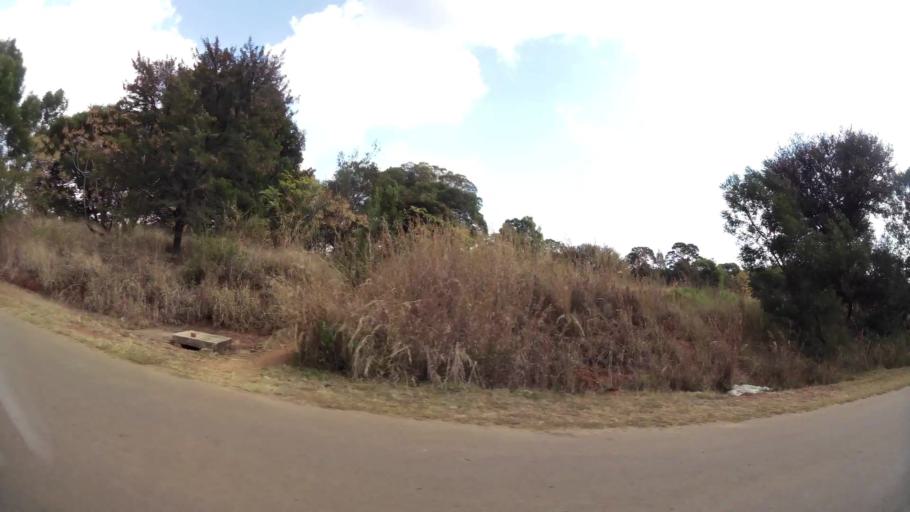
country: ZA
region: Gauteng
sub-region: City of Tshwane Metropolitan Municipality
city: Centurion
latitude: -25.8224
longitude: 28.2428
